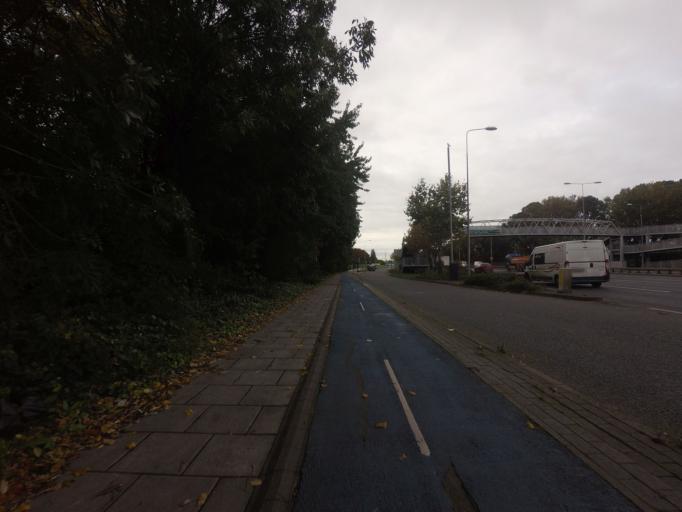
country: GB
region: England
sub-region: Greater London
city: Barking
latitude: 51.5238
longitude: 0.0699
